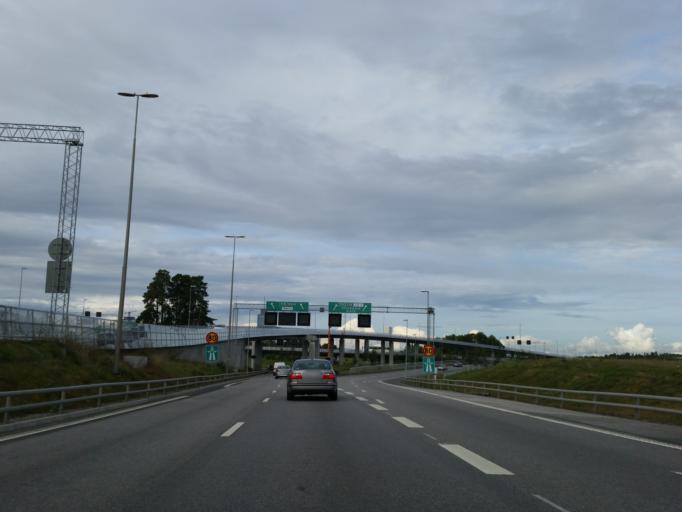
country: SE
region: Stockholm
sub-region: Stockholms Kommun
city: Kista
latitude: 59.3861
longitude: 17.9392
